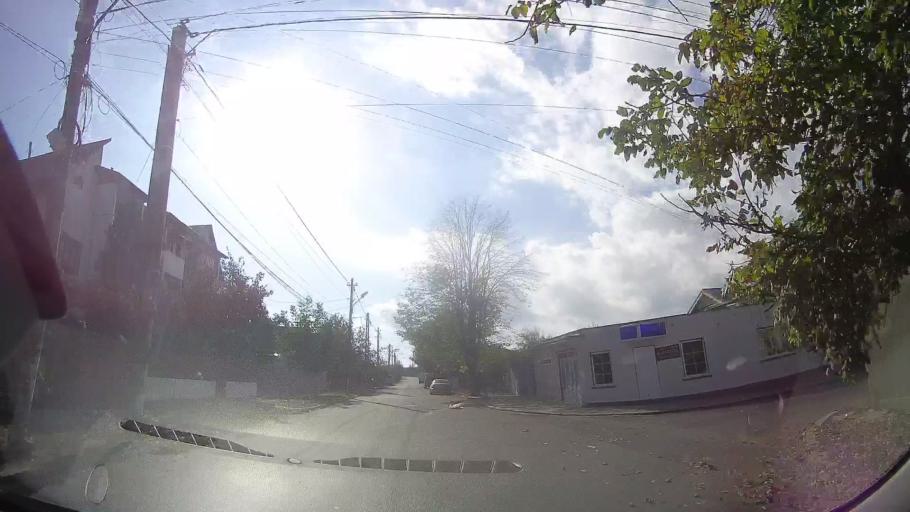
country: RO
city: Eforie Sud
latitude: 44.0198
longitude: 28.6484
